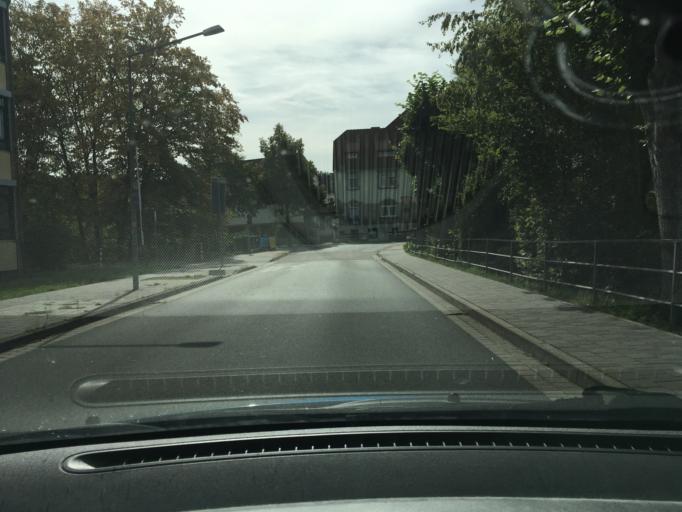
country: DE
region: Lower Saxony
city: Bad Munder am Deister
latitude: 52.1944
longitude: 9.4610
